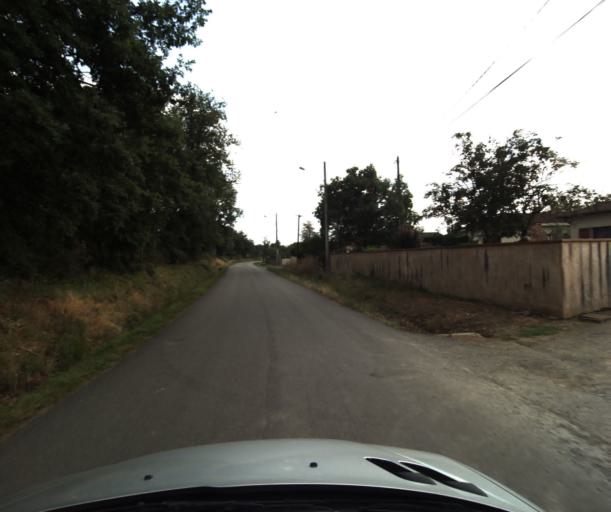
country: FR
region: Midi-Pyrenees
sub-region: Departement de la Haute-Garonne
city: Saint-Lys
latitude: 43.4981
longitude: 1.2027
